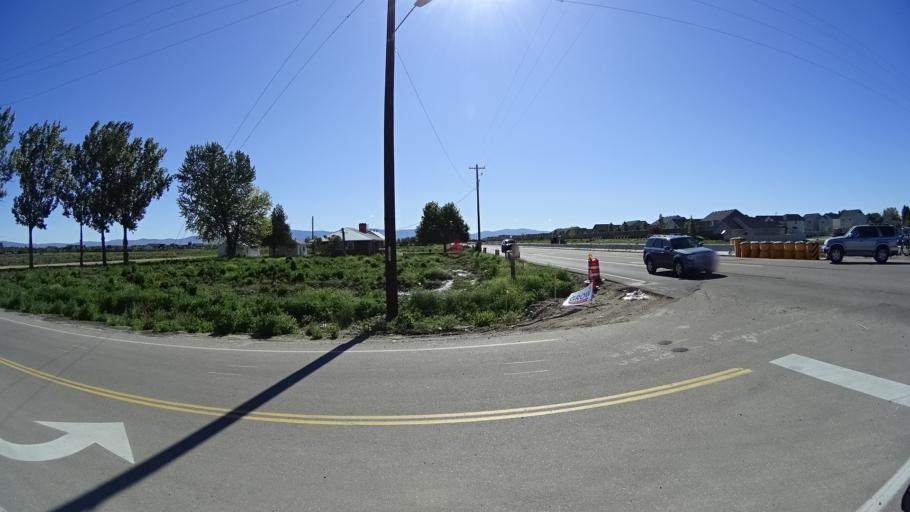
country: US
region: Idaho
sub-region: Ada County
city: Star
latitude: 43.6631
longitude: -116.4537
